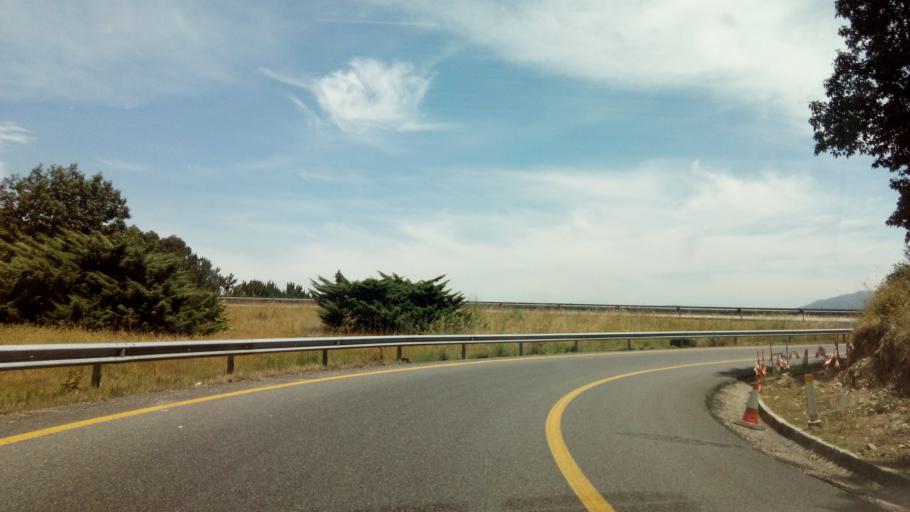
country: ES
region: Galicia
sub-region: Provincia de Pontevedra
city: Redondela
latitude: 42.2964
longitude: -8.6583
